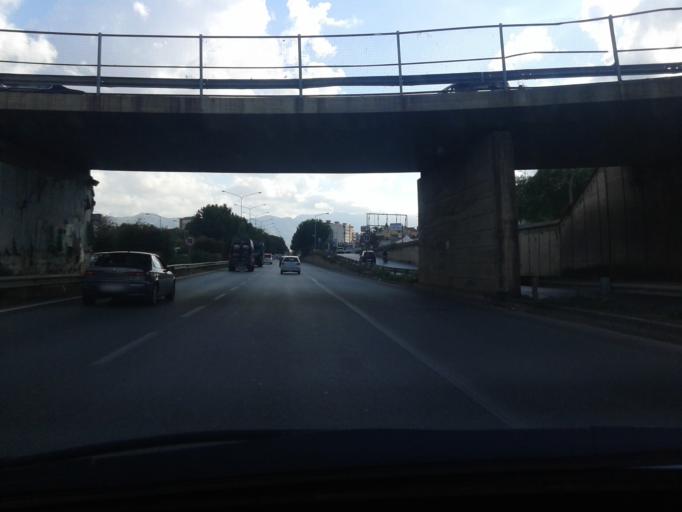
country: IT
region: Sicily
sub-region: Palermo
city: Palermo
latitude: 38.1394
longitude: 13.3311
